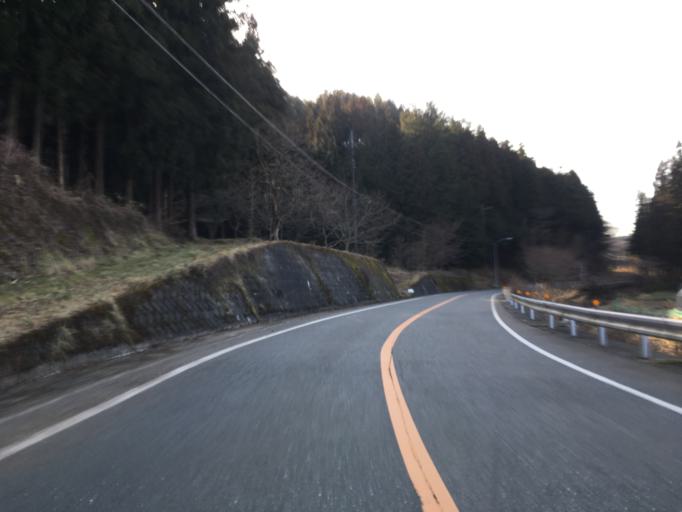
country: JP
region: Ibaraki
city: Takahagi
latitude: 36.7421
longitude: 140.5995
